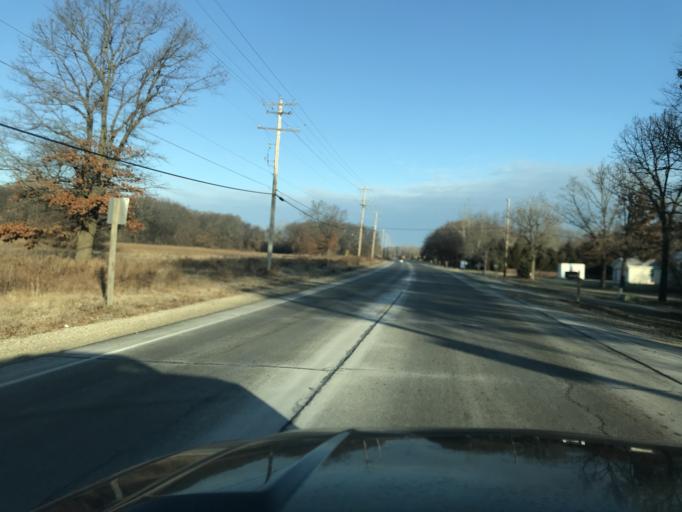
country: US
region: Illinois
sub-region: Lake County
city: Winthrop Harbor
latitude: 42.5254
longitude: -87.8245
